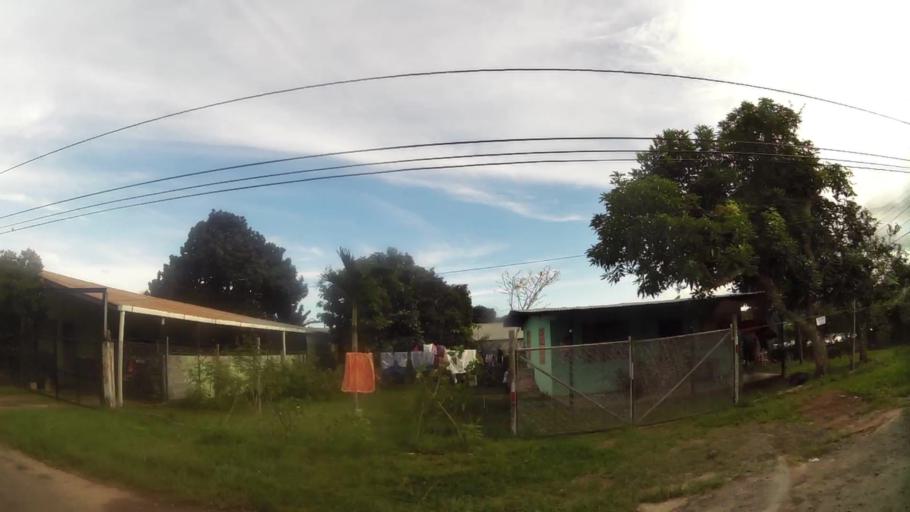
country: PA
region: Panama
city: El Coco
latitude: 8.8750
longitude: -79.8060
